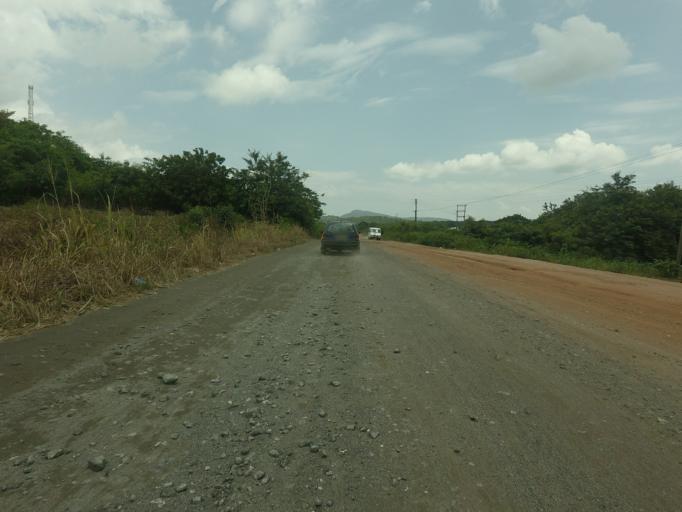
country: GH
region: Volta
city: Ho
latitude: 6.6792
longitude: 0.3203
